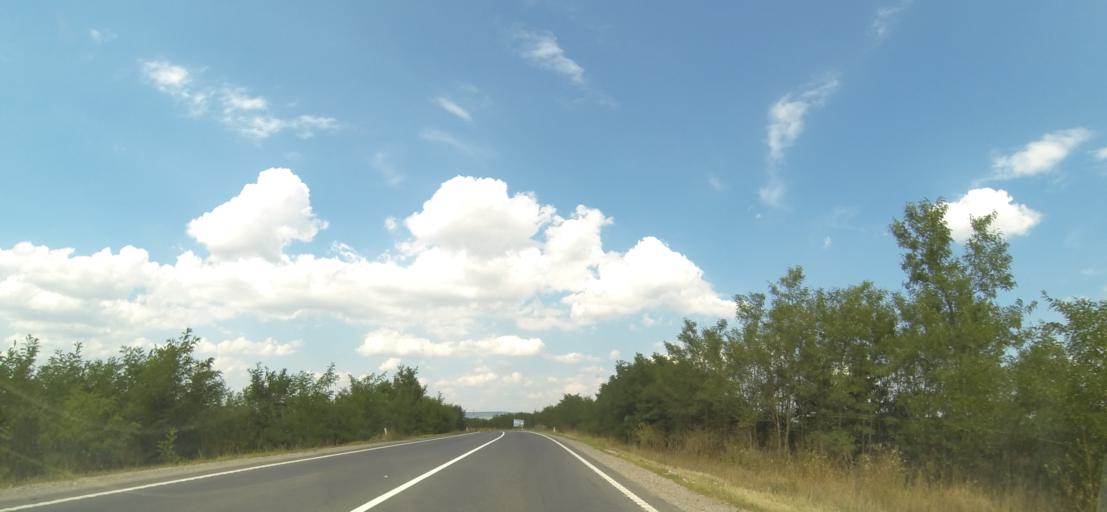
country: RO
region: Brasov
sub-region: Comuna Sercaia
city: Sercaia
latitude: 45.8213
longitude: 25.1580
